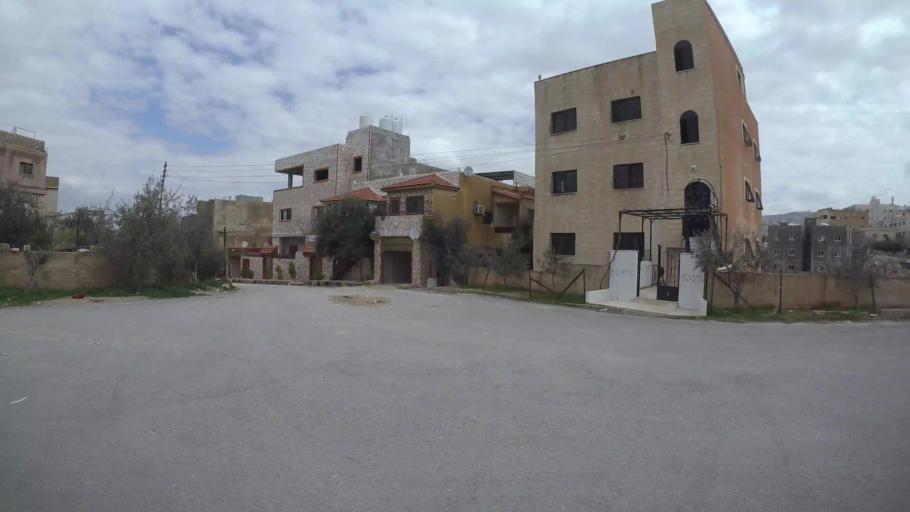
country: JO
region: Amman
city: Al Jubayhah
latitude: 32.0556
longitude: 35.8274
